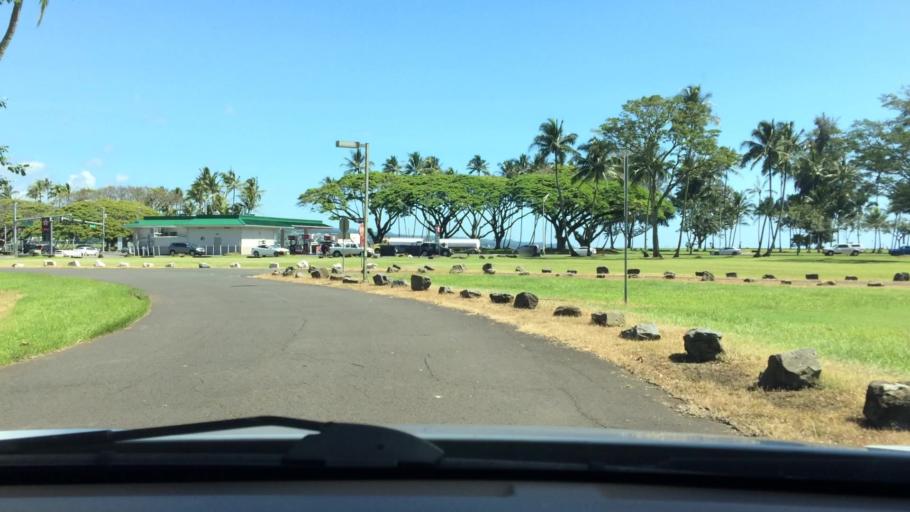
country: US
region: Hawaii
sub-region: Hawaii County
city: Hilo
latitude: 19.7209
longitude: -155.0778
